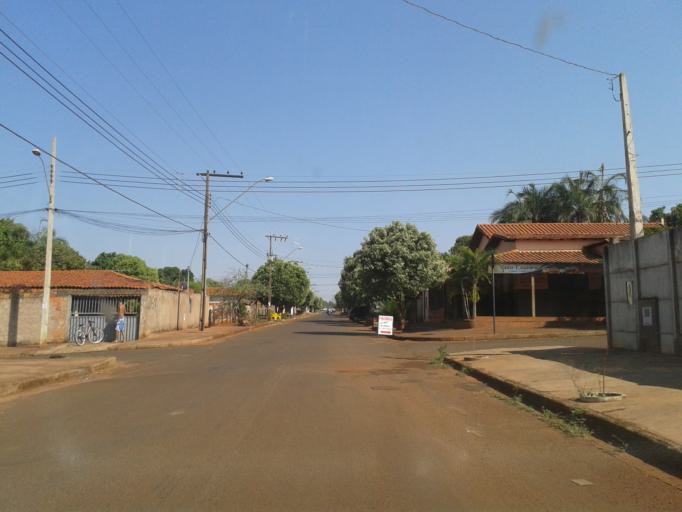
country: BR
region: Minas Gerais
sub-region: Ituiutaba
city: Ituiutaba
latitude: -18.9628
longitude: -49.4811
